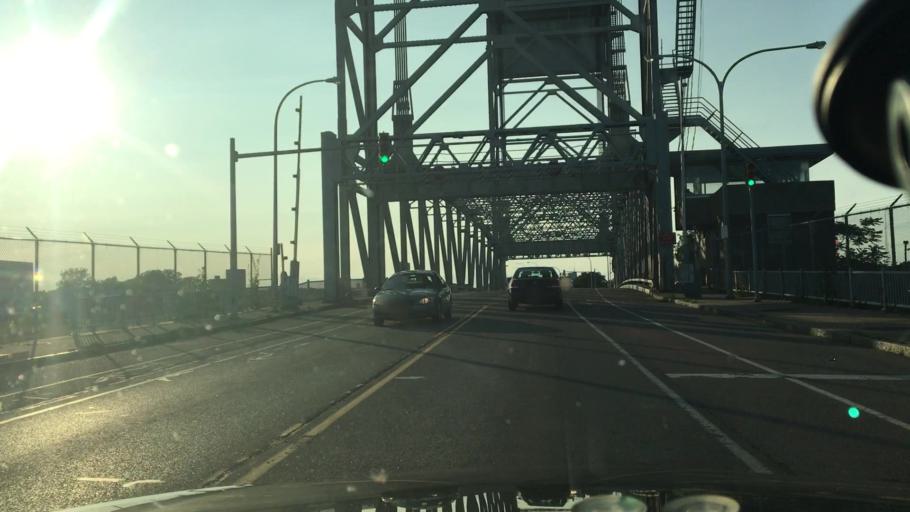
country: US
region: New York
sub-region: Erie County
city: Lackawanna
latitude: 42.8625
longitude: -78.8420
